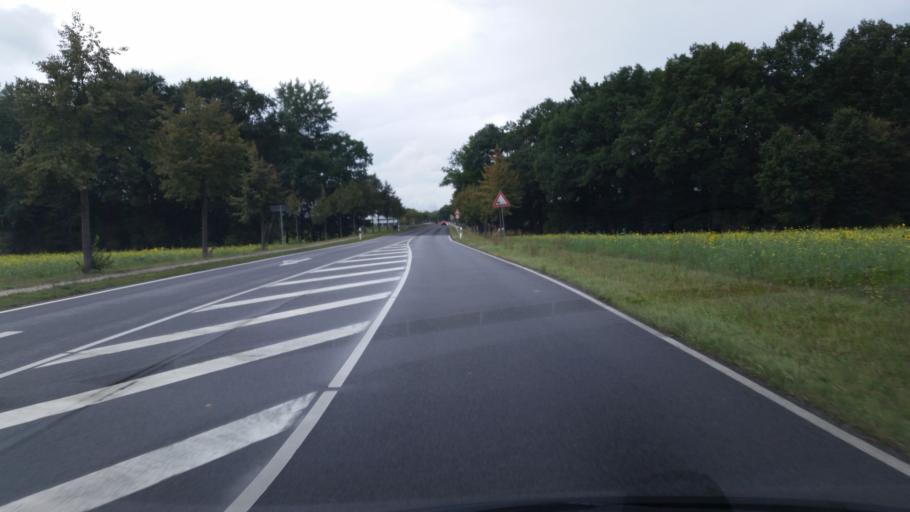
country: DE
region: Saxony
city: Kamenz
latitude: 51.2929
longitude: 14.1086
